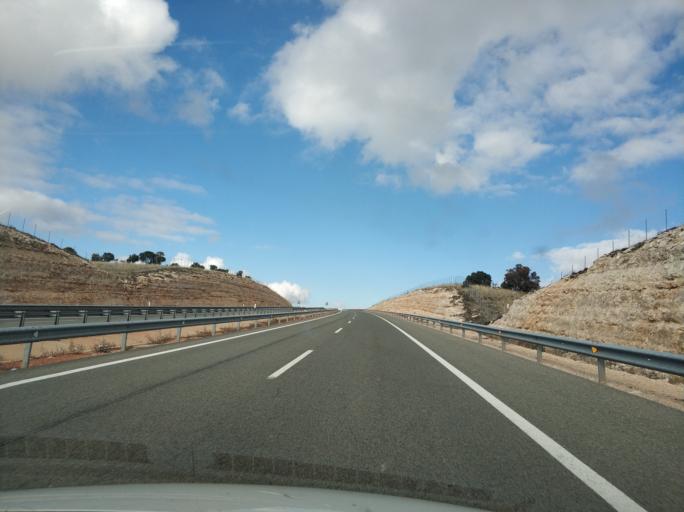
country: ES
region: Castille and Leon
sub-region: Provincia de Soria
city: Adradas
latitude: 41.2940
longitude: -2.4766
